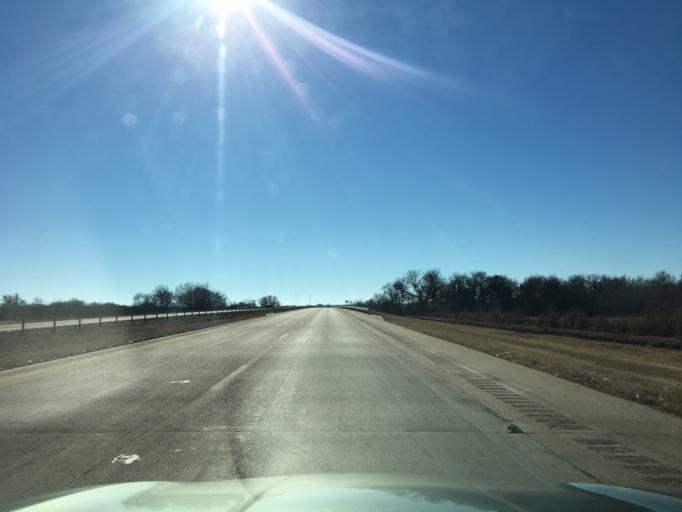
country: US
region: Oklahoma
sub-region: Kay County
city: Blackwell
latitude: 36.9108
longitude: -97.3525
